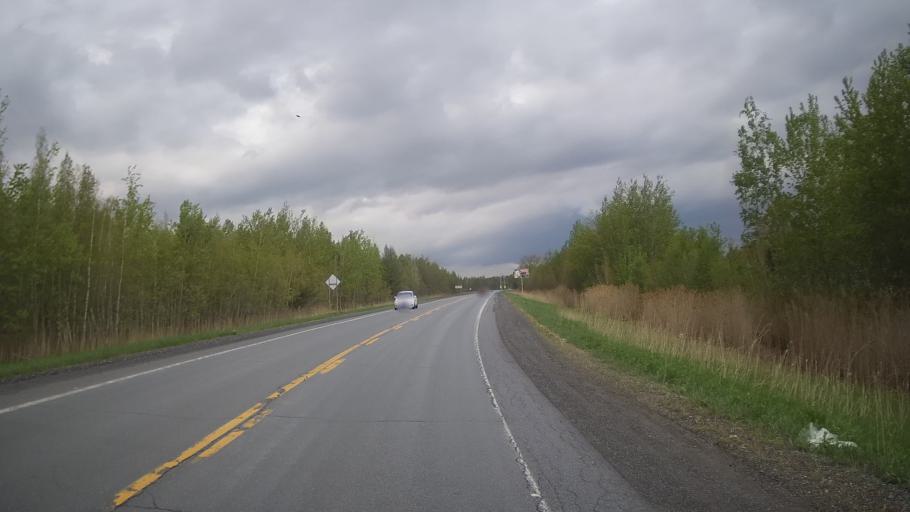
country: CA
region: Quebec
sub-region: Monteregie
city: Farnham
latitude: 45.2771
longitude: -72.9929
